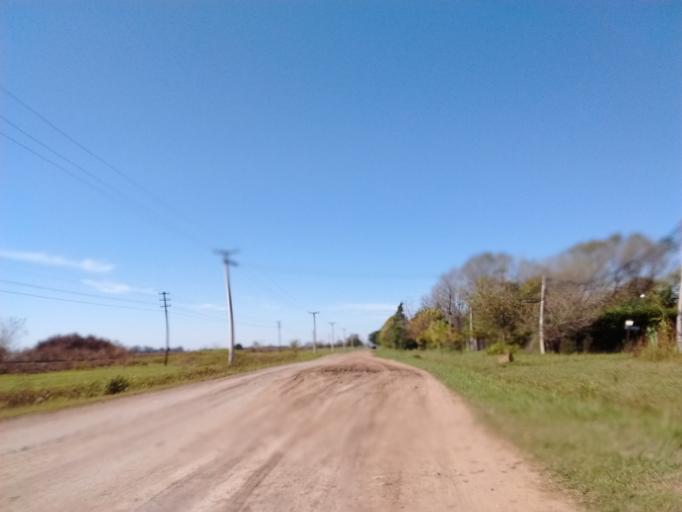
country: AR
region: Santa Fe
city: Funes
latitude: -32.9103
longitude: -60.8498
